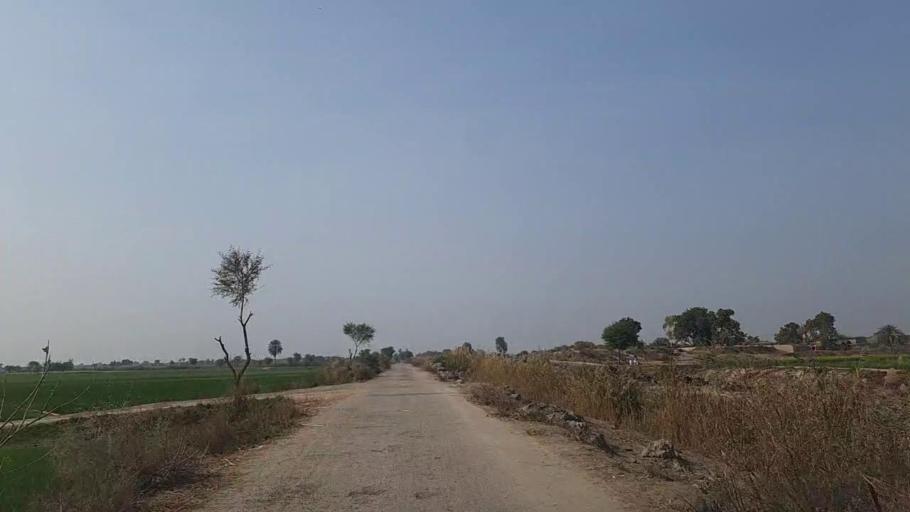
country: PK
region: Sindh
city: Daur
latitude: 26.5046
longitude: 68.4396
